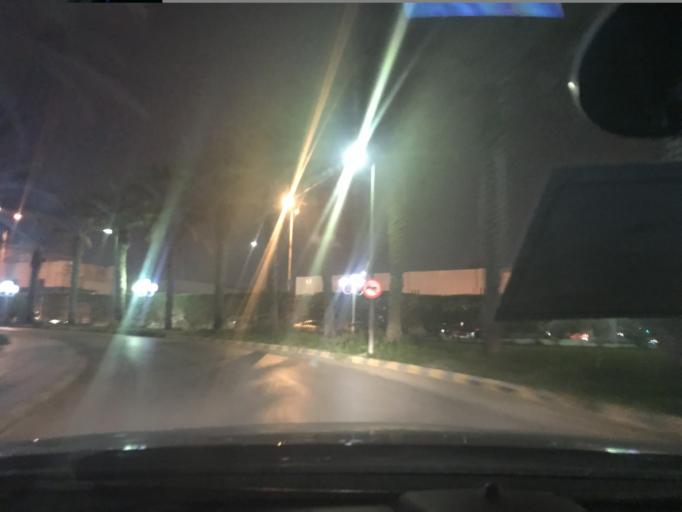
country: SA
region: Ar Riyad
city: Riyadh
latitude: 24.7023
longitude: 46.7791
